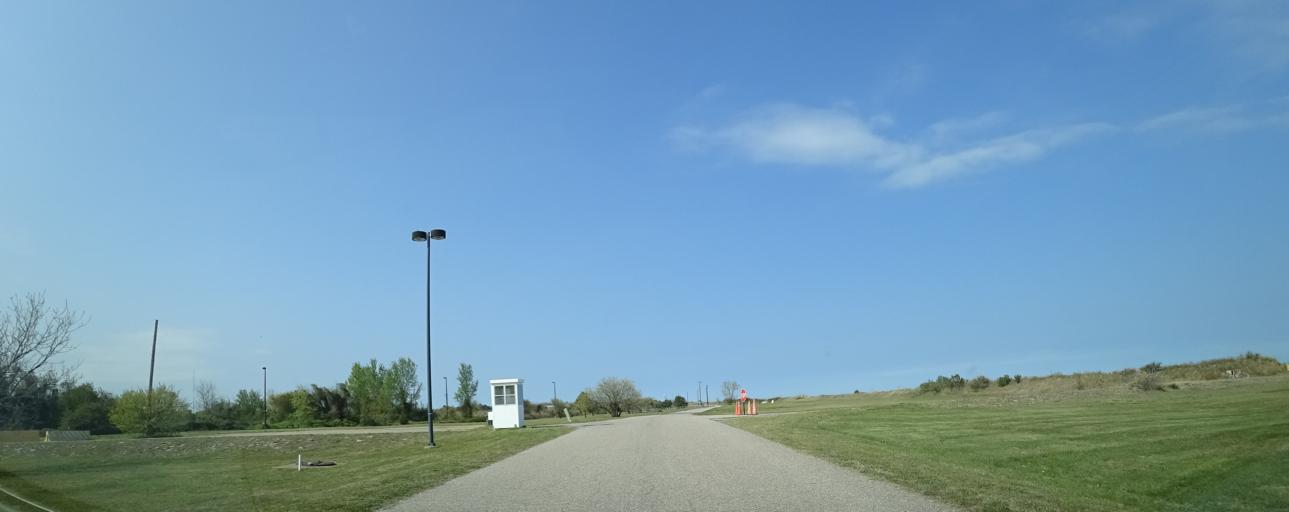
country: US
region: Virginia
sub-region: City of Hampton
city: East Hampton
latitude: 37.0247
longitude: -76.2974
